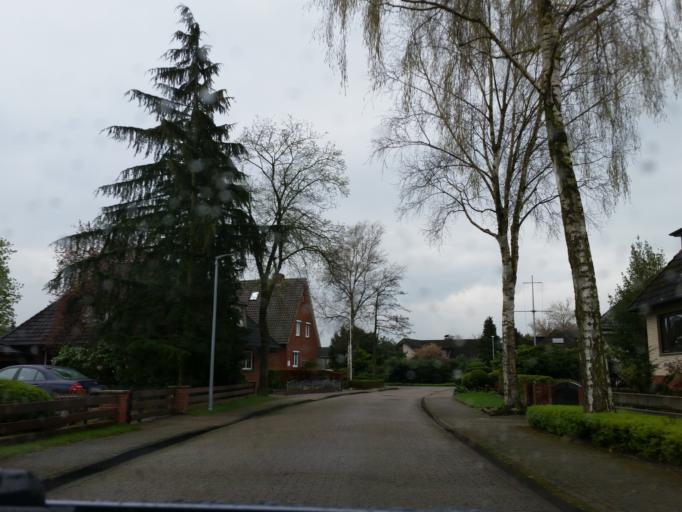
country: DE
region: Lower Saxony
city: Bremervorde
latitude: 53.4892
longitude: 9.1545
